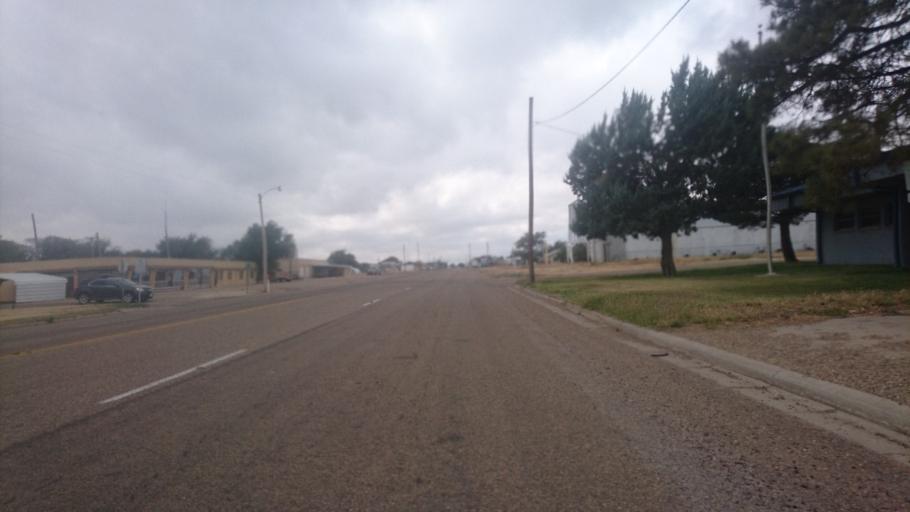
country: US
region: Texas
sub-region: Oldham County
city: Vega
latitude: 35.2431
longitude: -102.4241
